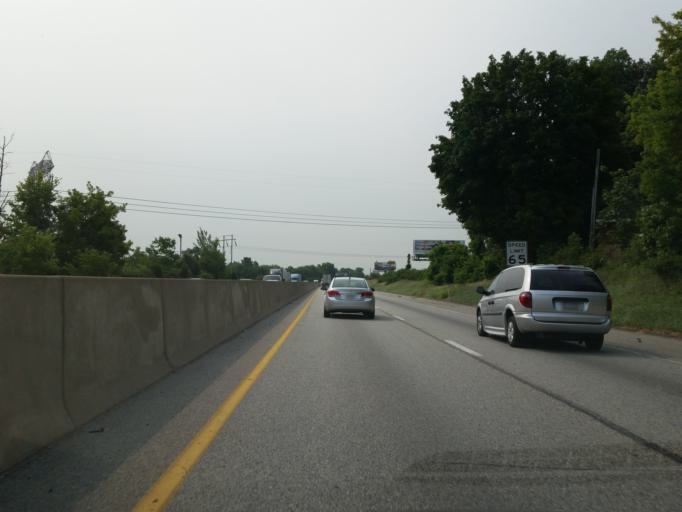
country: US
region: Pennsylvania
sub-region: York County
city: Manchester
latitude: 40.0753
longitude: -76.7609
